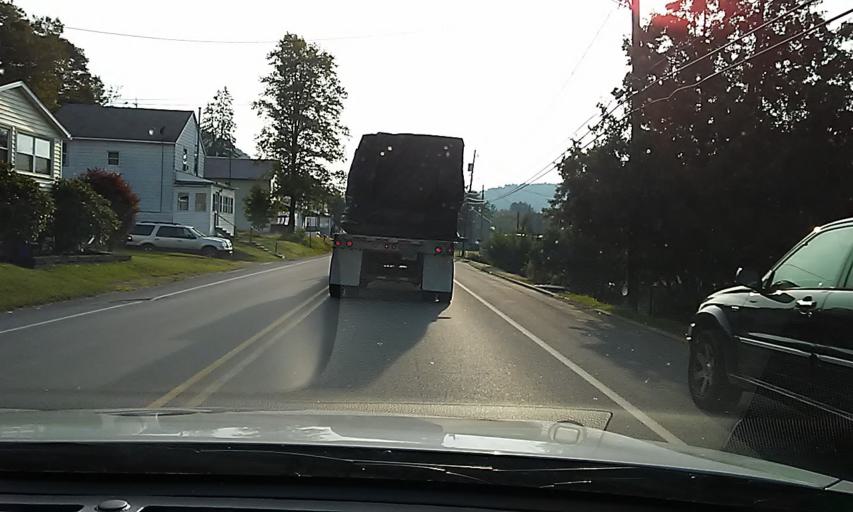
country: US
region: Pennsylvania
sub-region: McKean County
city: Smethport
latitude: 41.7060
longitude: -78.5792
